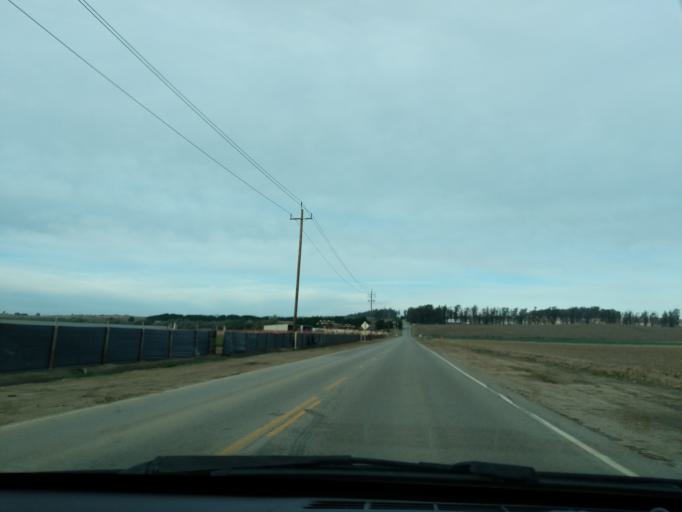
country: US
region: California
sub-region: Santa Barbara County
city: Guadalupe
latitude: 35.0133
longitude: -120.5666
